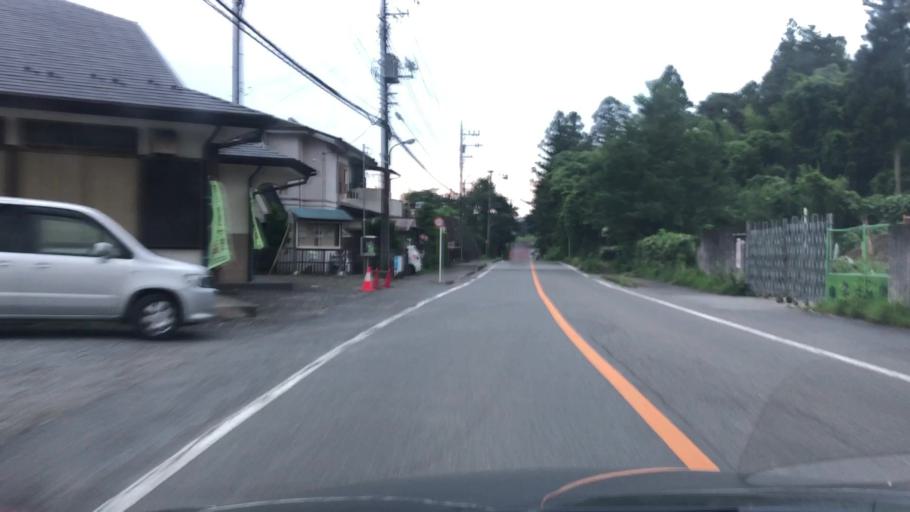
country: JP
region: Tokyo
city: Ome
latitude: 35.7560
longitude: 139.2361
